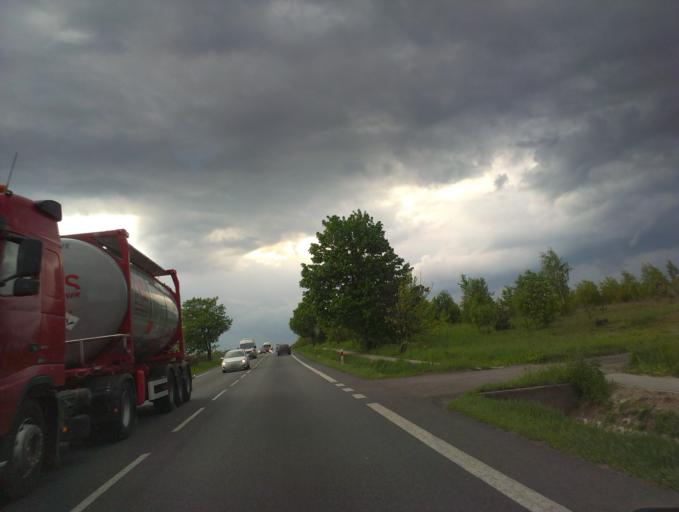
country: PL
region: Masovian Voivodeship
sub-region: Powiat grojecki
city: Pniewy
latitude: 51.9003
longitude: 20.7701
